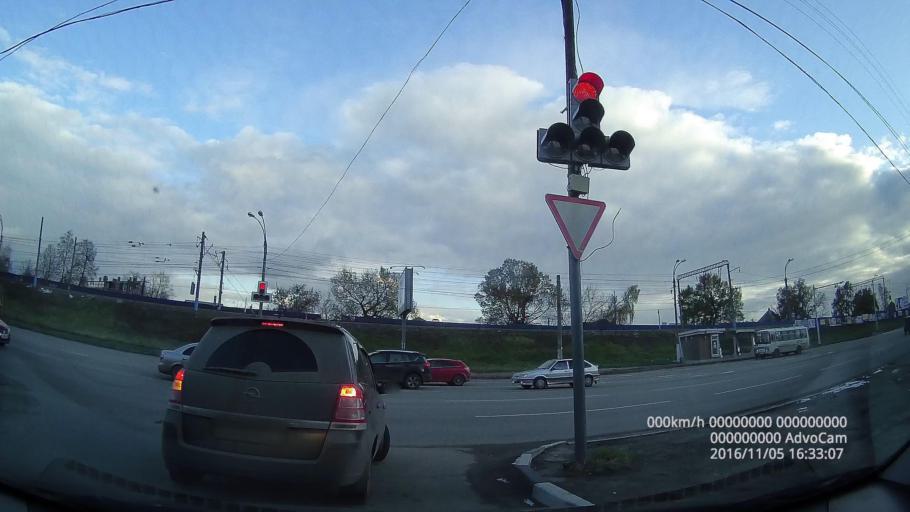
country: RU
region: Voronezj
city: Voronezh
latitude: 51.6820
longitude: 39.2155
